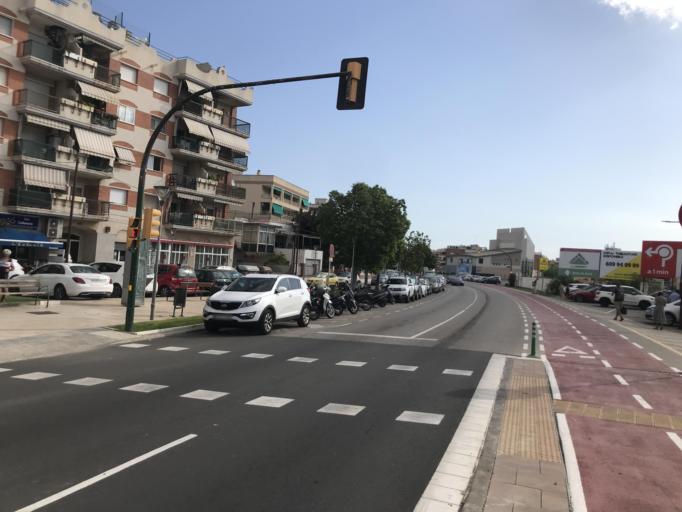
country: ES
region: Catalonia
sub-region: Provincia de Tarragona
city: Torredembarra
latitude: 41.1430
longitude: 1.4056
